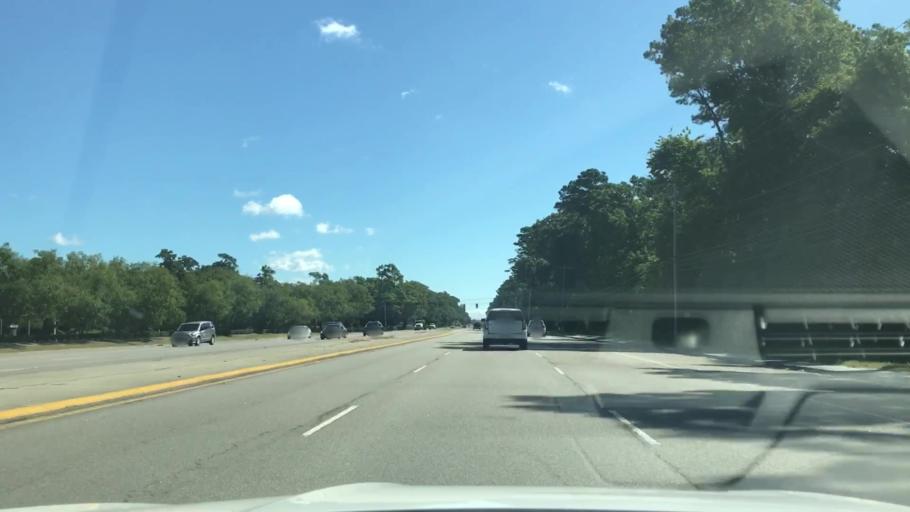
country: US
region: South Carolina
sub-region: Horry County
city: North Myrtle Beach
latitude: 33.7904
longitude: -78.7650
